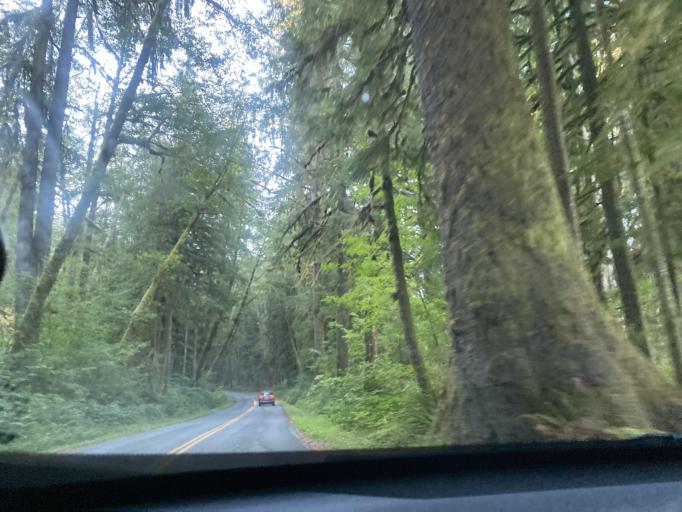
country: US
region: Washington
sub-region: Clallam County
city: Forks
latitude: 47.8159
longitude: -124.1092
